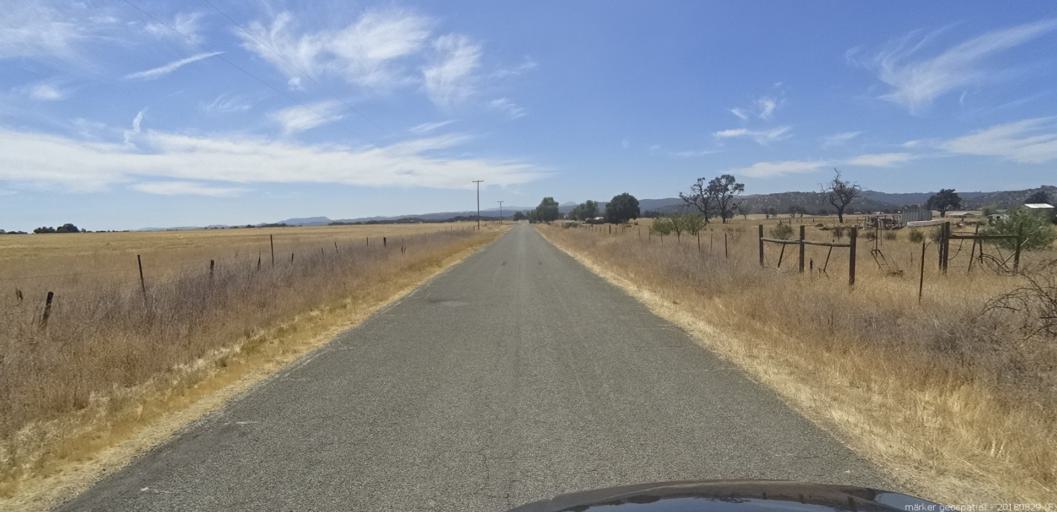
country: US
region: California
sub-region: San Luis Obispo County
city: Lake Nacimiento
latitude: 35.9349
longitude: -121.0642
